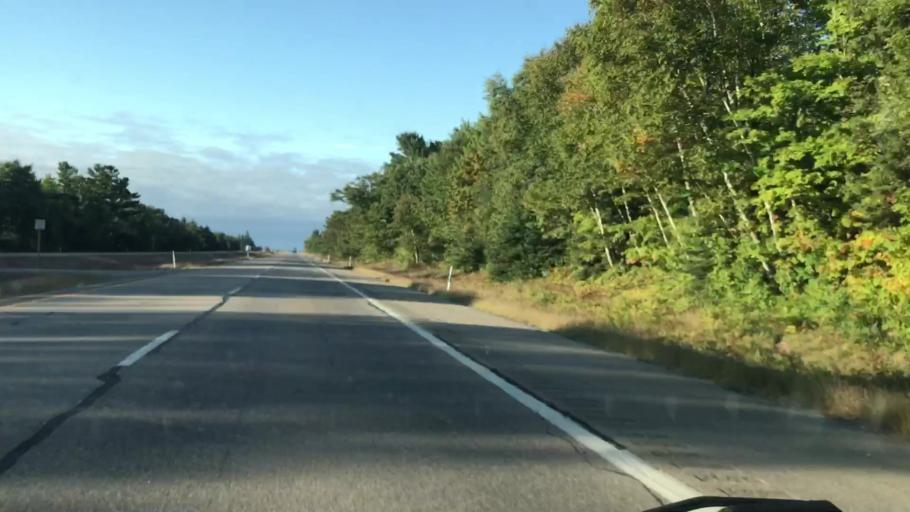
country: US
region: Michigan
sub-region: Chippewa County
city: Sault Ste. Marie
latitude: 46.4344
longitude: -84.3894
